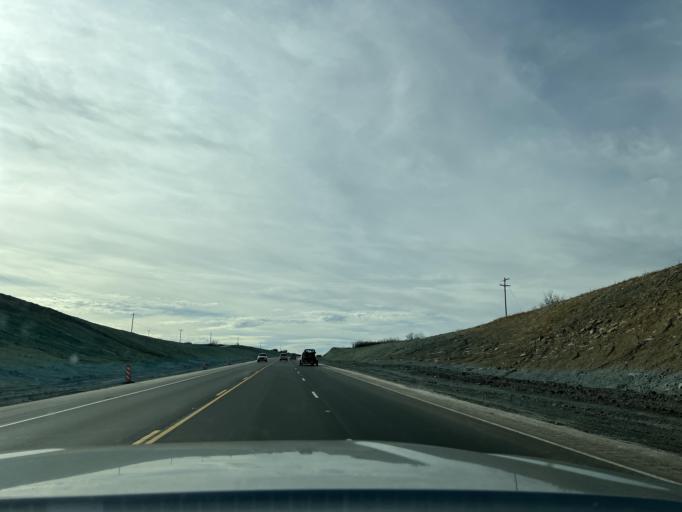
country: US
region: Texas
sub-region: Shackelford County
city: Albany
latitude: 32.7078
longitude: -99.3759
